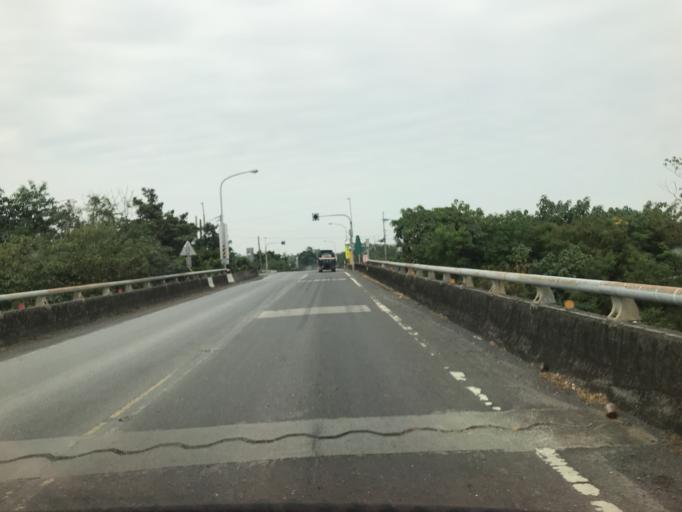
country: TW
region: Taiwan
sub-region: Pingtung
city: Pingtung
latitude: 22.4938
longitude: 120.5926
